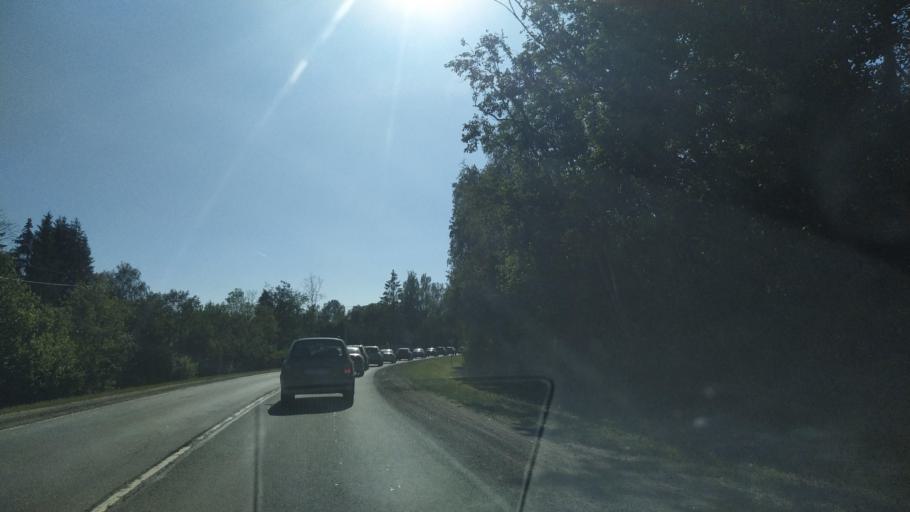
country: RU
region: Leningrad
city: Kirovsk
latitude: 59.9254
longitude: 30.9739
